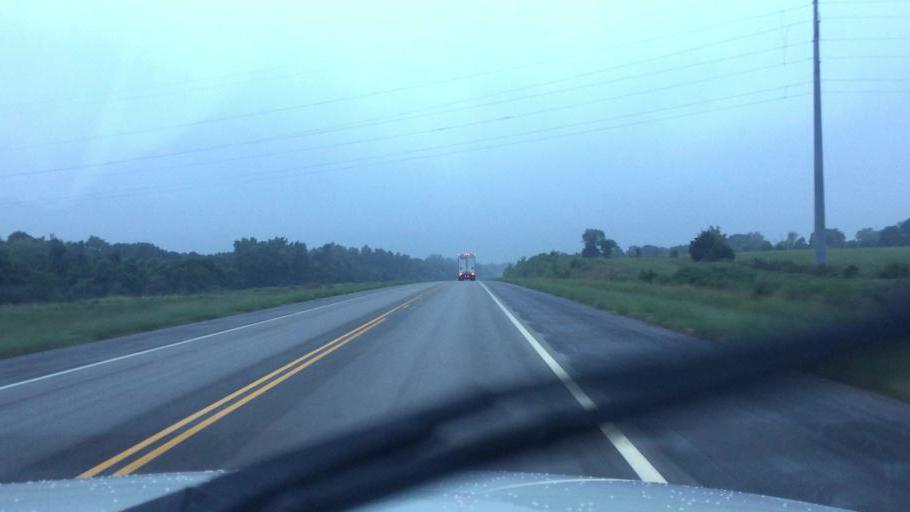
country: US
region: Kansas
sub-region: Montgomery County
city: Cherryvale
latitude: 37.4516
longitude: -95.4831
